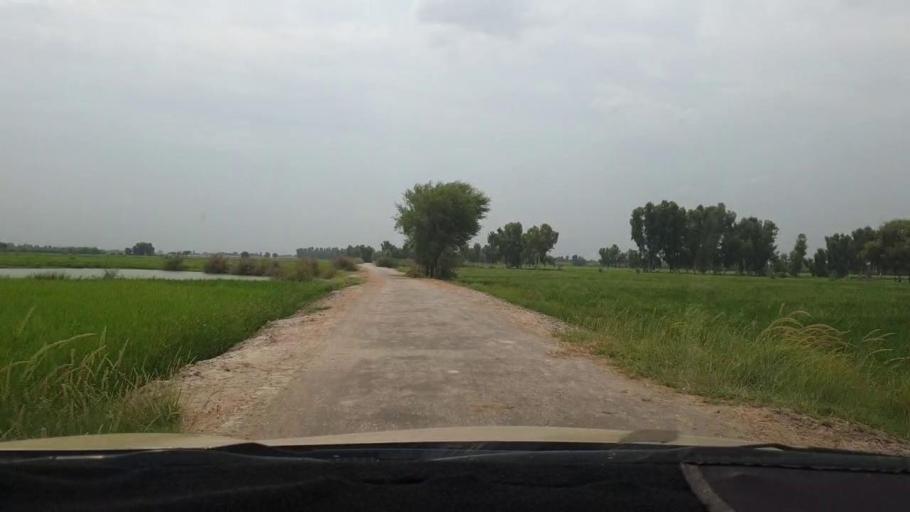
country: PK
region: Sindh
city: Naudero
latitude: 27.6267
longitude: 68.3209
